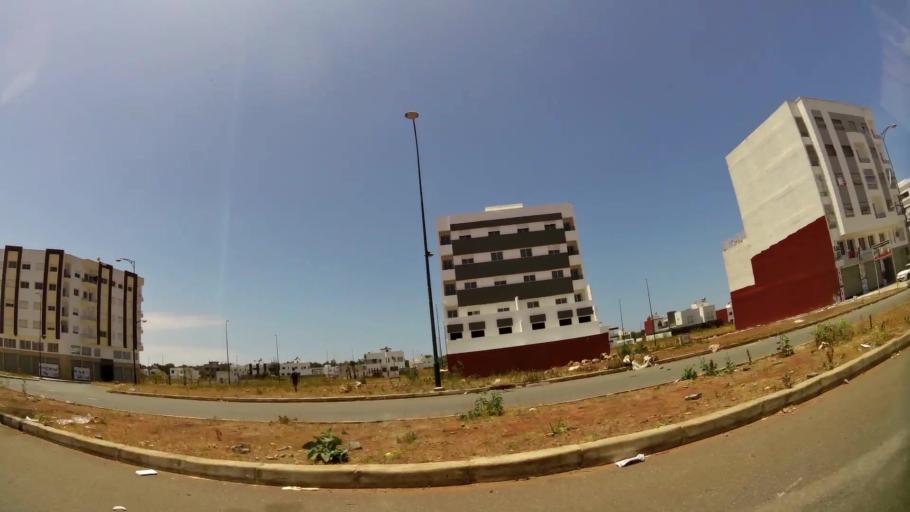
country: MA
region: Gharb-Chrarda-Beni Hssen
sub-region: Kenitra Province
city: Kenitra
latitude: 34.2678
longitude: -6.6270
